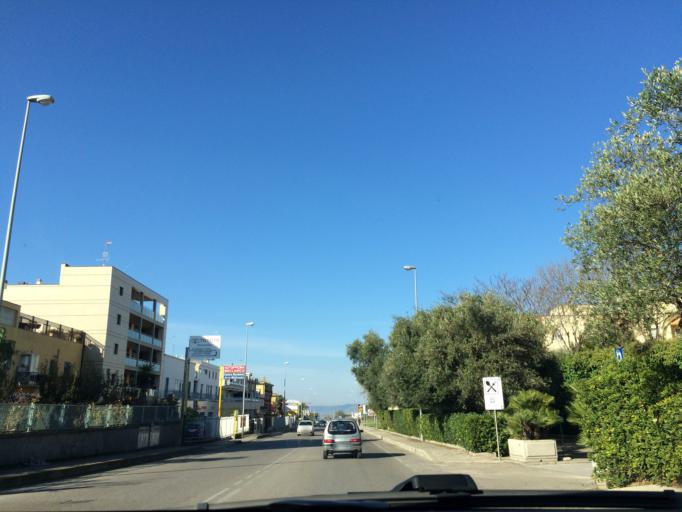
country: IT
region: Basilicate
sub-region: Provincia di Matera
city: Matera
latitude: 40.6807
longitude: 16.5838
